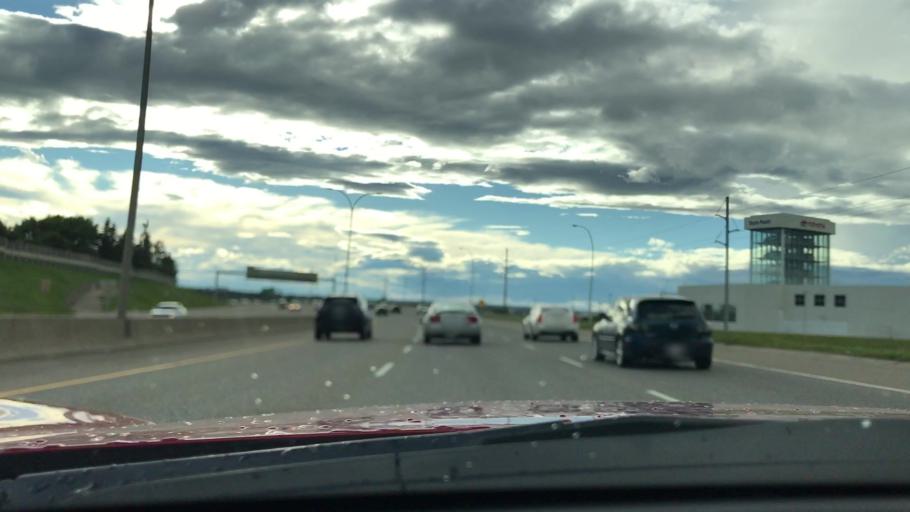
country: CA
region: Alberta
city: Calgary
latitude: 50.9453
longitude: -113.9831
